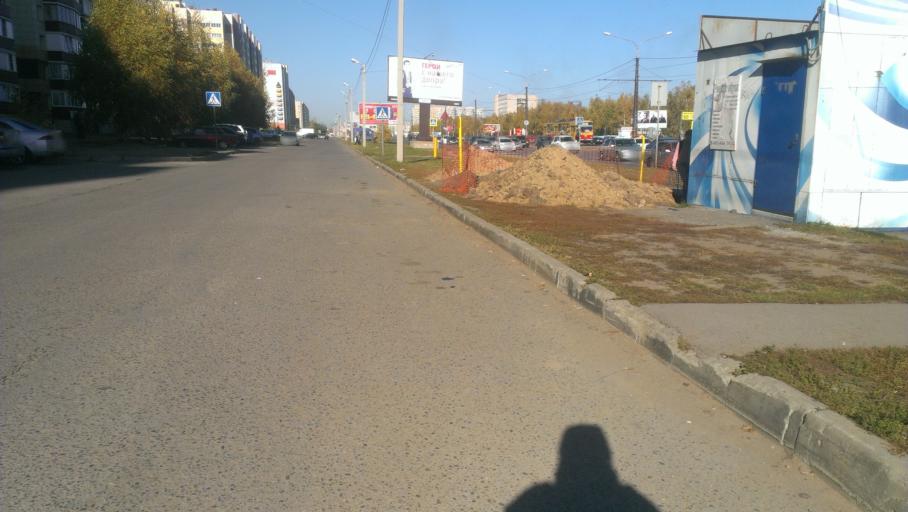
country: RU
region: Altai Krai
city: Novosilikatnyy
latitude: 53.3301
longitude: 83.6922
